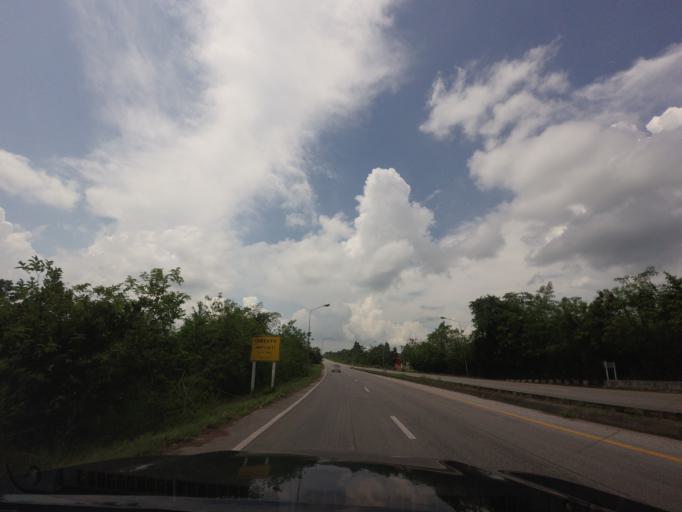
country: TH
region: Khon Kaen
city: Phu Wiang
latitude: 16.6804
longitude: 102.3497
